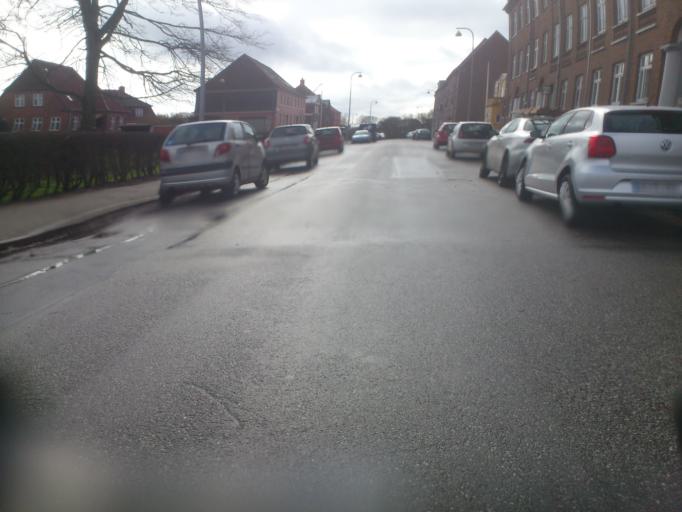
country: DK
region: South Denmark
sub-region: Fredericia Kommune
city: Fredericia
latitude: 55.5615
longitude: 9.7656
